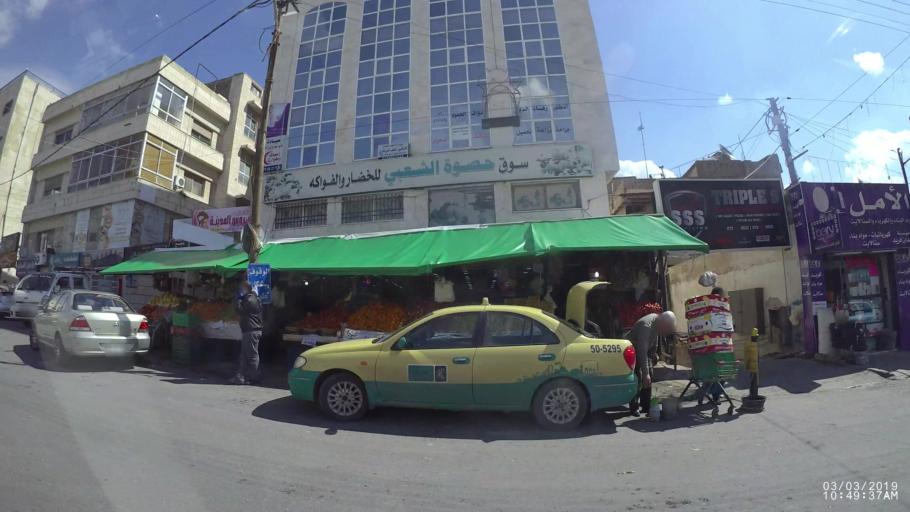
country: JO
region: Amman
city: Amman
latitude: 31.9883
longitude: 35.9035
